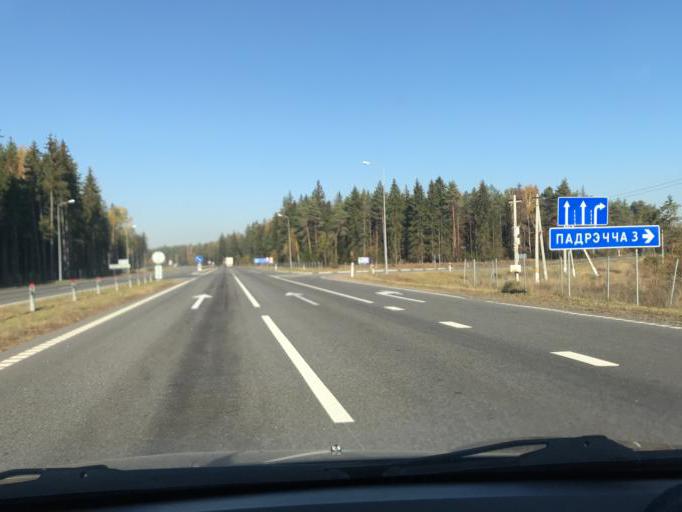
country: BY
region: Mogilev
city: Kirawsk
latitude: 53.2179
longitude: 29.3416
